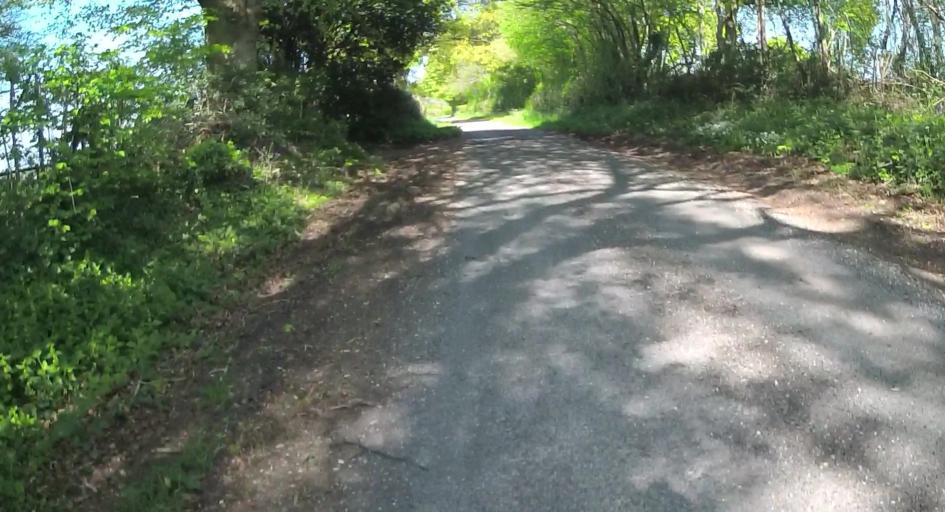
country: GB
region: England
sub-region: Hampshire
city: Four Marks
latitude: 51.1382
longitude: -1.0396
